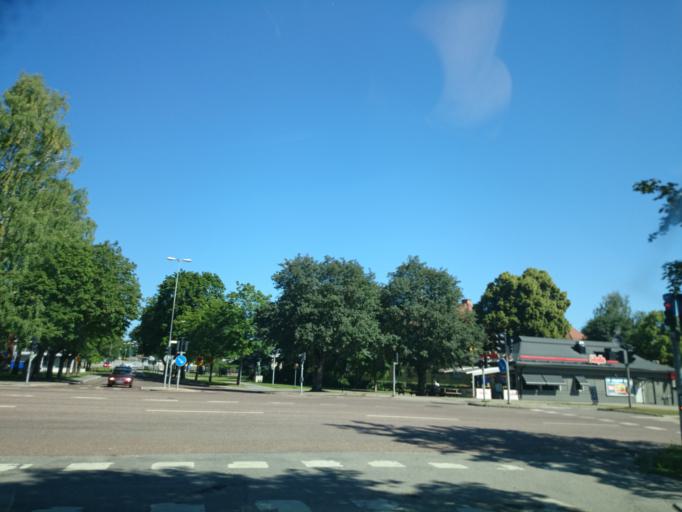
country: SE
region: Gaevleborg
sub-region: Gavle Kommun
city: Gavle
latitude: 60.6754
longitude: 17.1209
